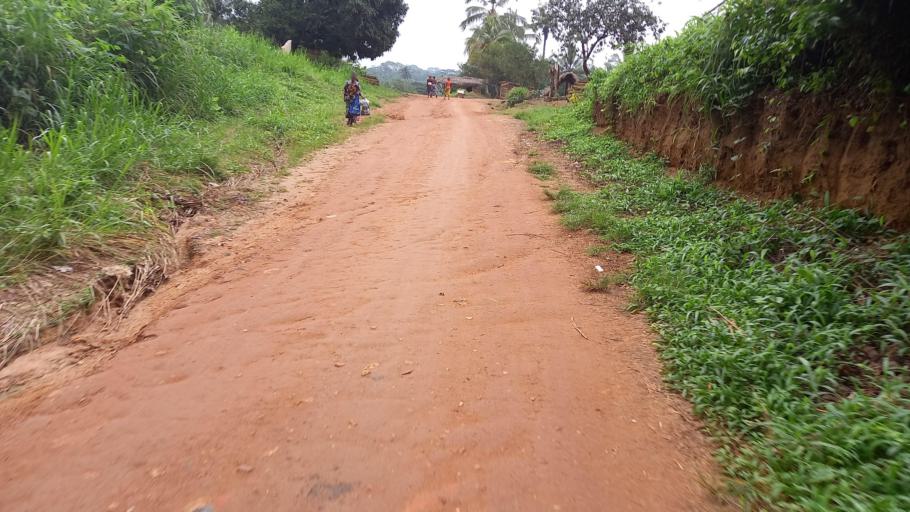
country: SL
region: Eastern Province
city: Kailahun
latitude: 8.2489
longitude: -10.5192
